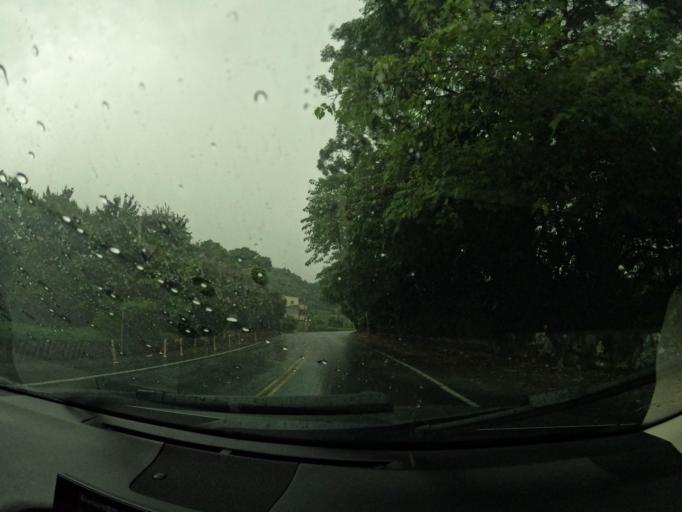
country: TW
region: Taiwan
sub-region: Nantou
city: Nantou
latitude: 23.8830
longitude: 120.7568
